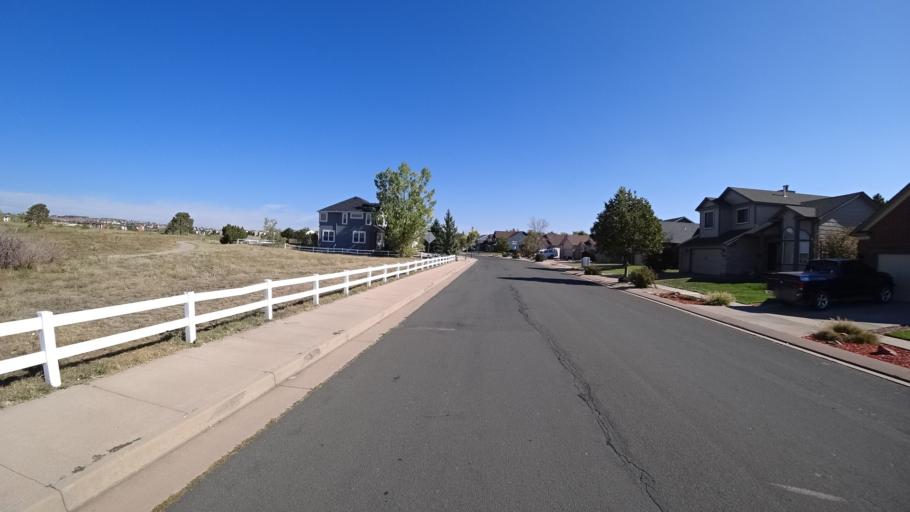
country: US
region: Colorado
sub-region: El Paso County
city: Cimarron Hills
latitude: 38.8793
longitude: -104.7084
